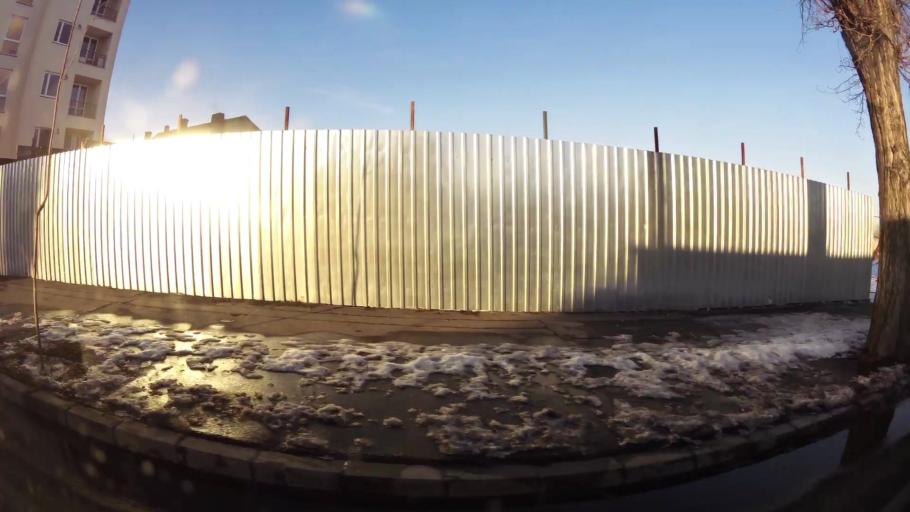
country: RO
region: Ilfov
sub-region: Comuna Fundeni-Dobroesti
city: Fundeni
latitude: 44.4528
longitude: 26.1335
